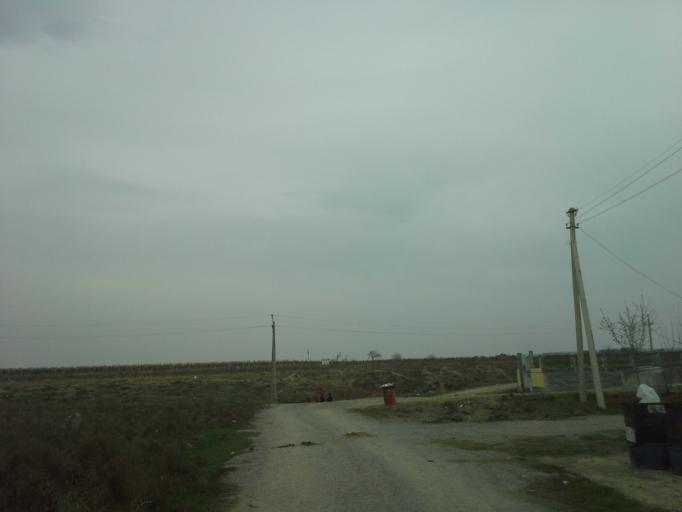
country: TM
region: Ahal
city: Abadan
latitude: 37.9792
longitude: 58.2257
